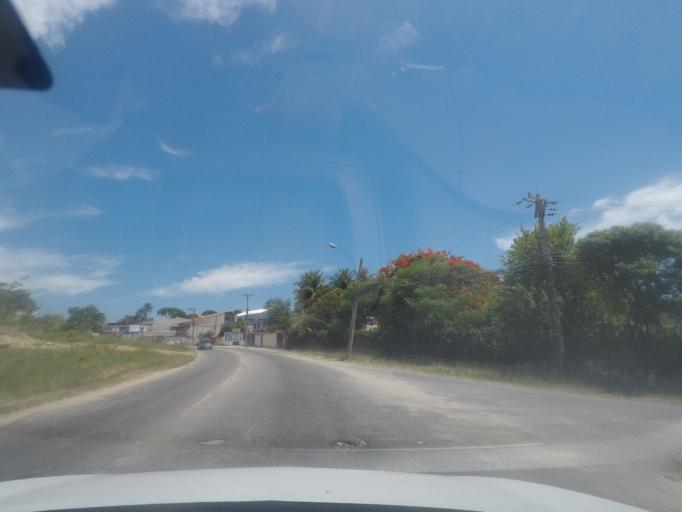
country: BR
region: Rio de Janeiro
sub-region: Itaguai
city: Itaguai
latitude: -22.9976
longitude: -43.6503
